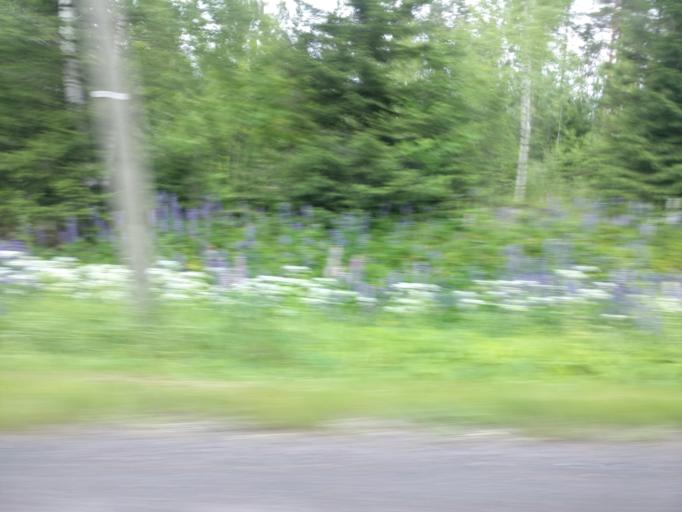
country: FI
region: Northern Savo
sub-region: Varkaus
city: Varkaus
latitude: 62.3482
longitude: 27.8191
